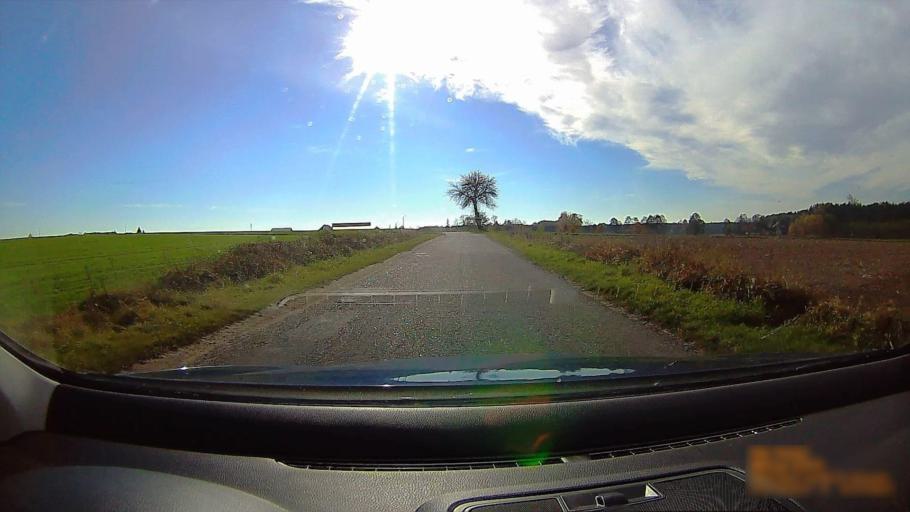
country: PL
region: Greater Poland Voivodeship
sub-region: Powiat ostrzeszowski
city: Doruchow
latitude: 51.3986
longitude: 18.0302
